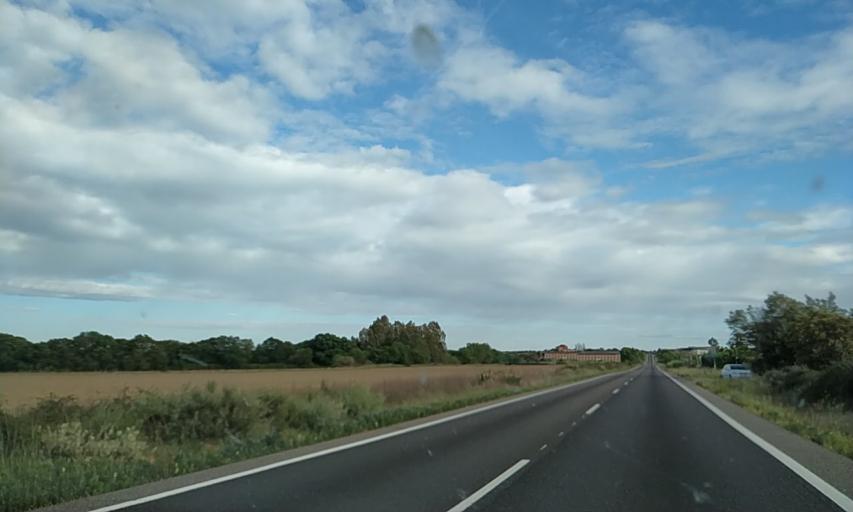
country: ES
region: Extremadura
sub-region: Provincia de Caceres
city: Huelaga
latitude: 40.0437
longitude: -6.6335
